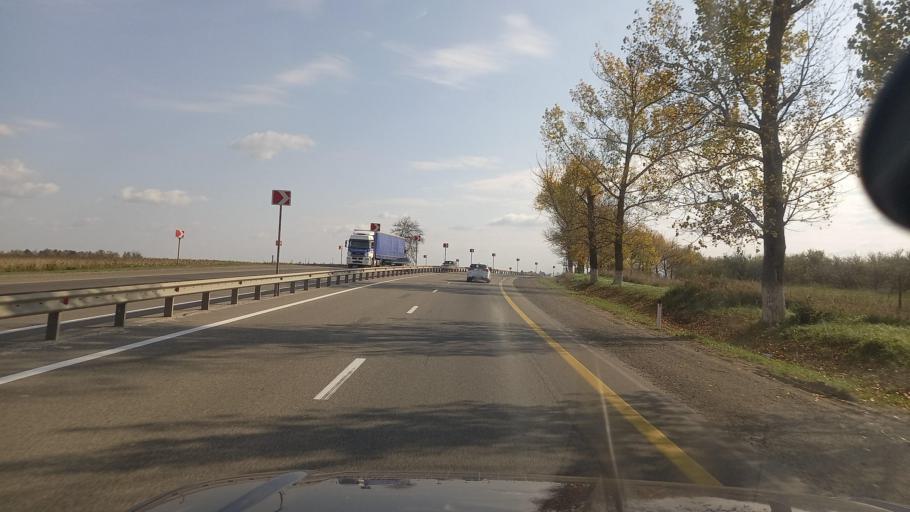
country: RU
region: Krasnodarskiy
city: Akhtyrskiy
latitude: 44.8542
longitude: 38.2621
